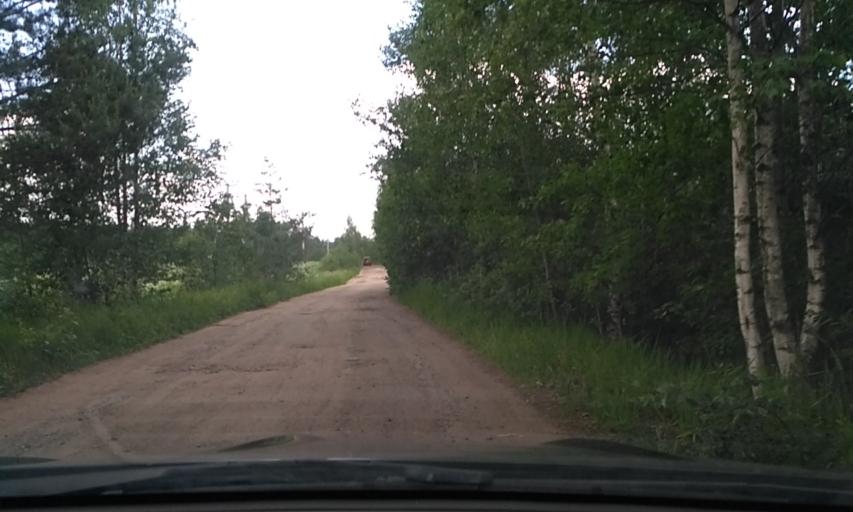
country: RU
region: Leningrad
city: Otradnoye
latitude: 59.8169
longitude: 30.8260
